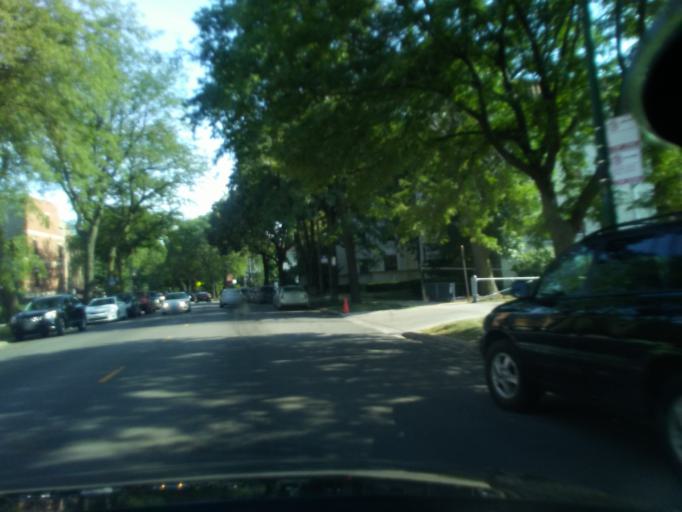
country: US
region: Illinois
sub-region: Cook County
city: Evanston
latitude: 42.0159
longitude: -87.6843
